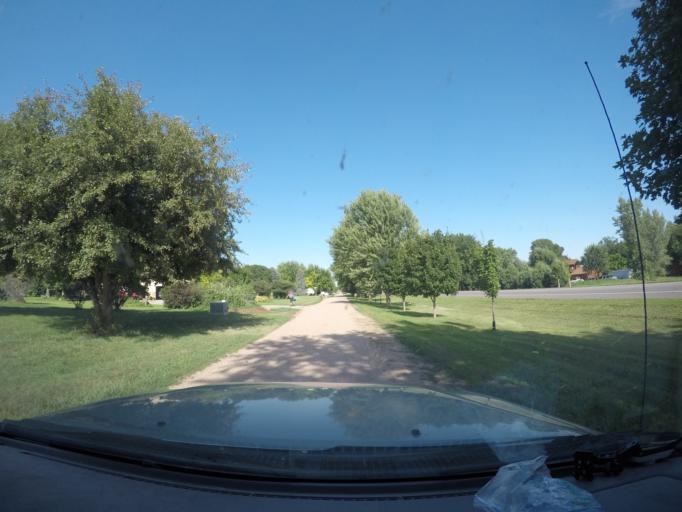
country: US
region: Nebraska
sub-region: Buffalo County
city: Kearney
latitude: 40.6997
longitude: -99.1721
